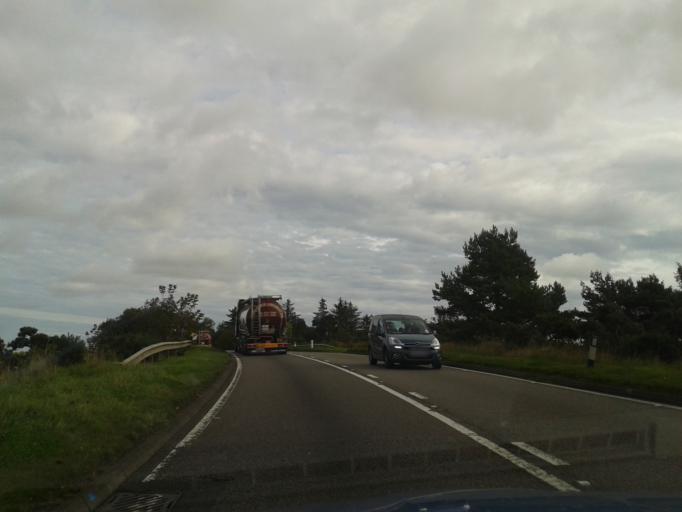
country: GB
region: Scotland
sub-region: Moray
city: Burghead
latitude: 57.6370
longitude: -3.4647
